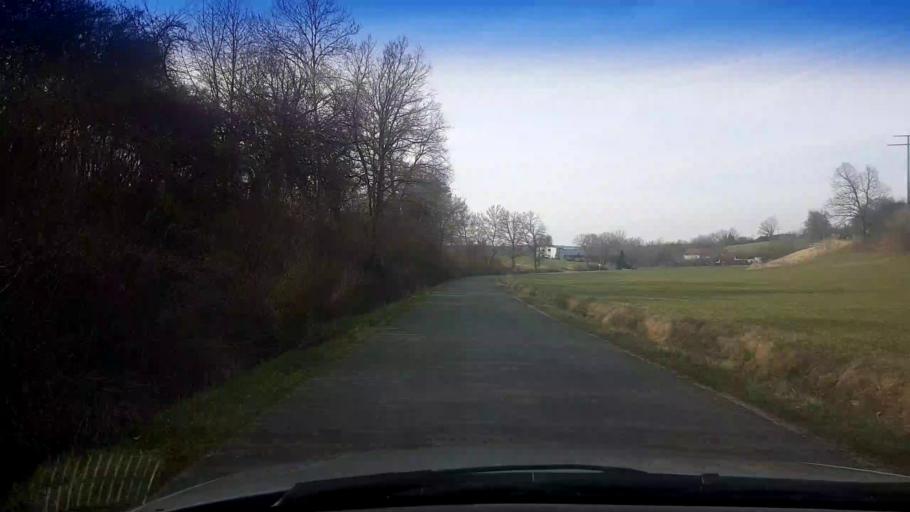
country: DE
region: Bavaria
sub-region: Upper Franconia
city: Burgebrach
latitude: 49.8150
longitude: 10.7506
